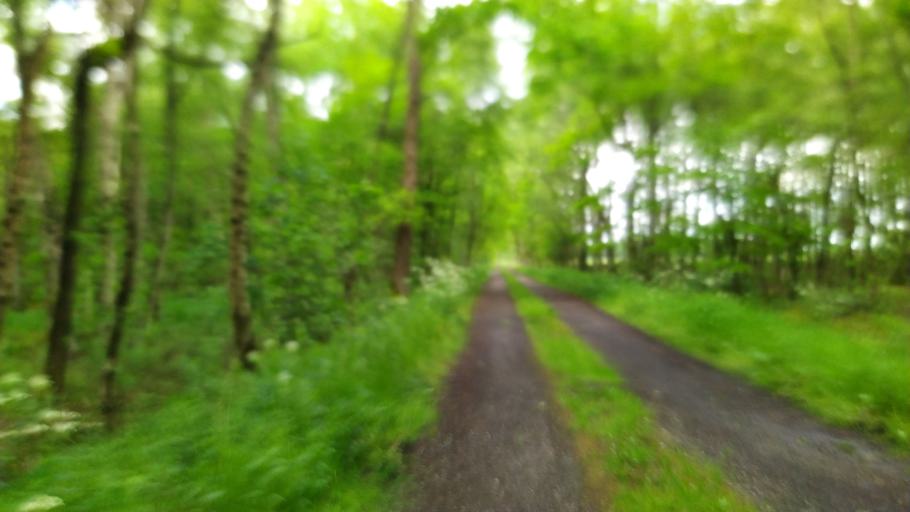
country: DE
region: Lower Saxony
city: Brest
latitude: 53.4227
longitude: 9.3570
